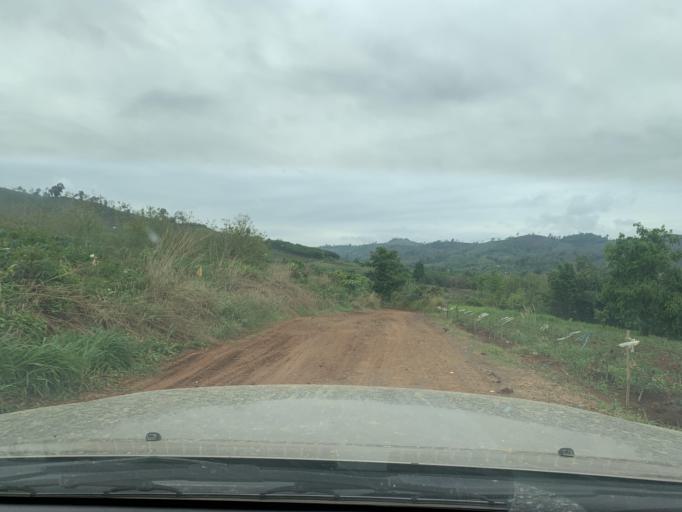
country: TH
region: Nan
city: Mae Charim
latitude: 18.4067
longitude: 101.4411
